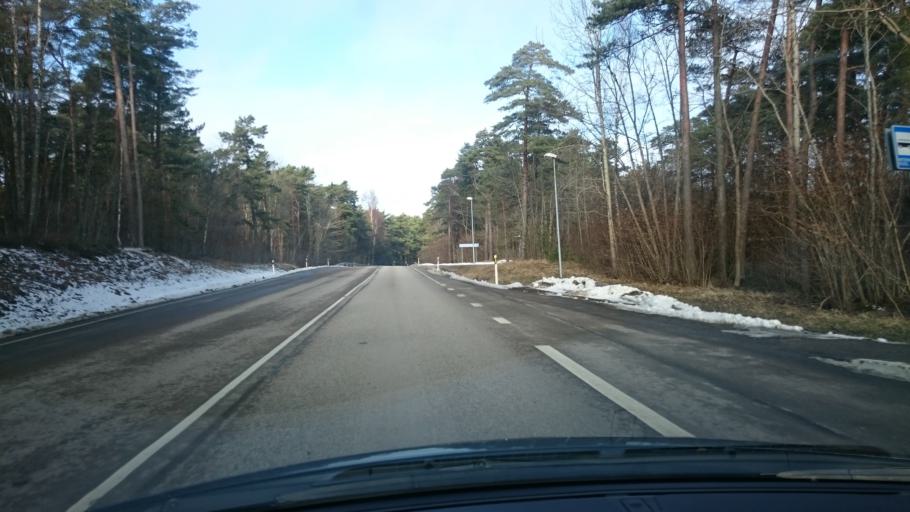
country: EE
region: Harju
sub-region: Keila linn
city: Keila
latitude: 59.4057
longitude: 24.2977
